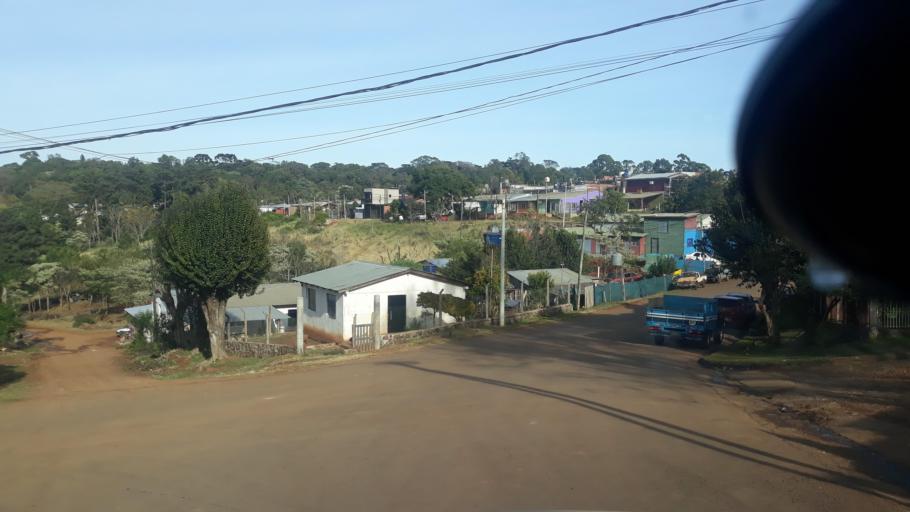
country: AR
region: Misiones
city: Bernardo de Irigoyen
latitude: -26.2656
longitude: -53.6523
